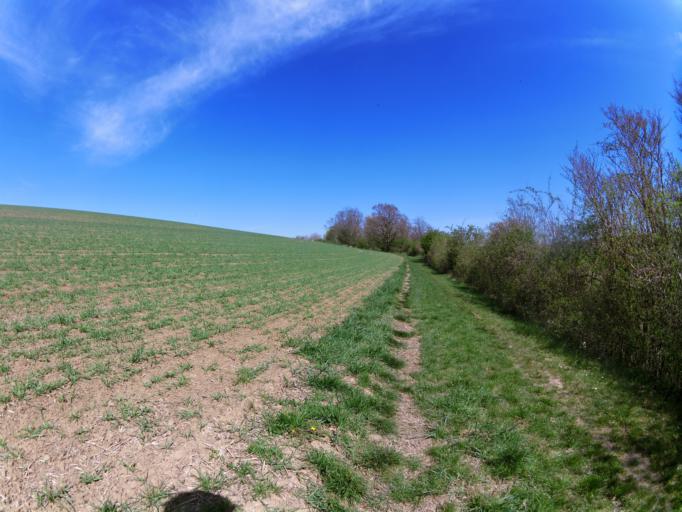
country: DE
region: Bavaria
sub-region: Regierungsbezirk Unterfranken
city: Winterhausen
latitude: 49.6956
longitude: 9.9980
